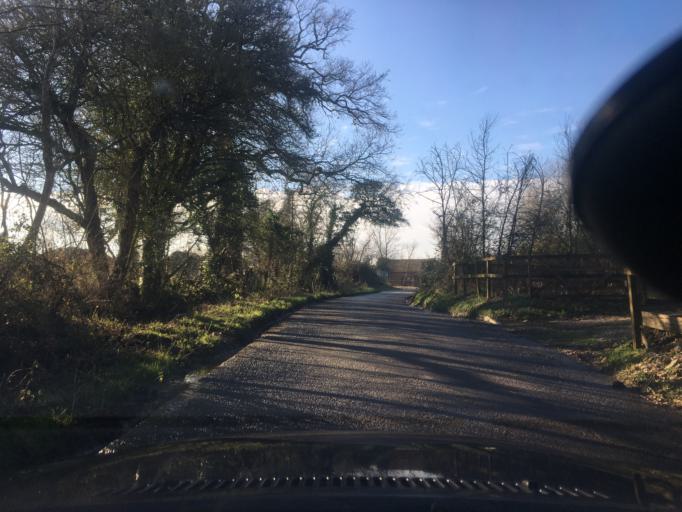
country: GB
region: England
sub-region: West Berkshire
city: Stratfield Mortimer
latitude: 51.3929
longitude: -1.0217
